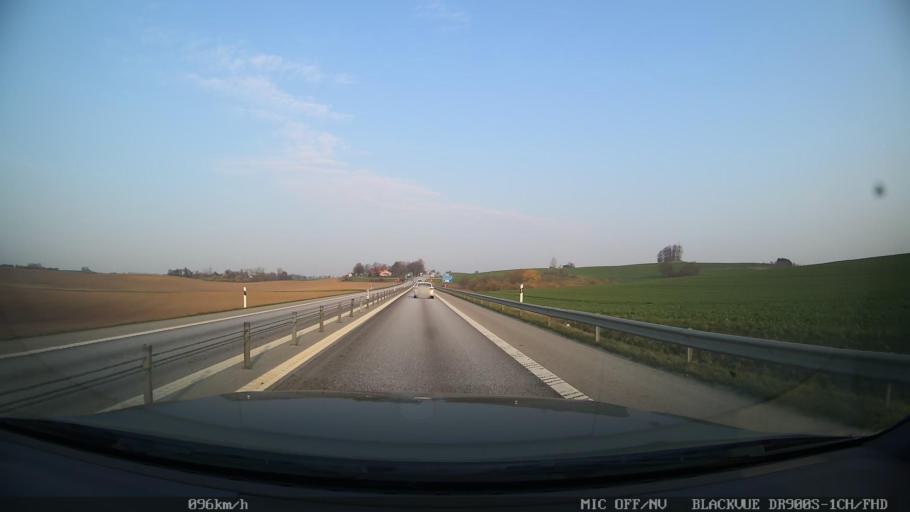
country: SE
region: Skane
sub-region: Ystads Kommun
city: Ystad
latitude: 55.4481
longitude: 13.7703
